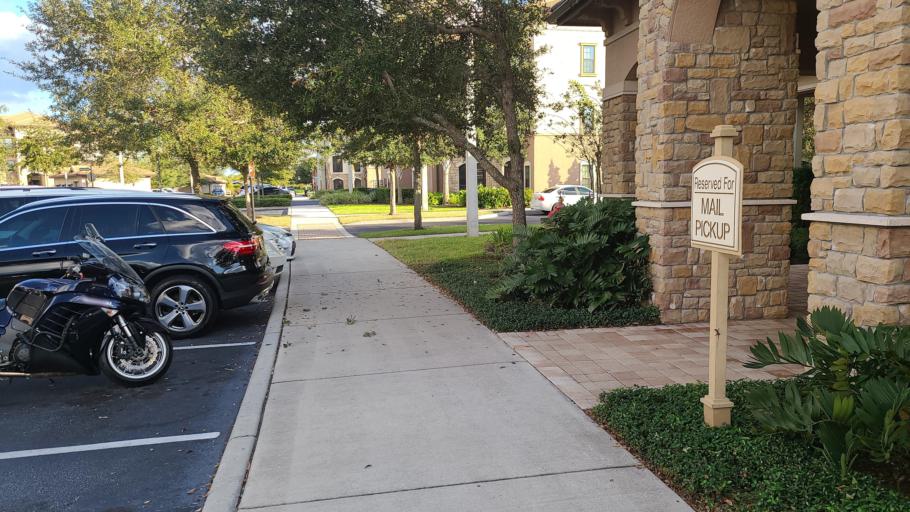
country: US
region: Florida
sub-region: Osceola County
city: Buenaventura Lakes
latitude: 28.3585
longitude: -81.2388
